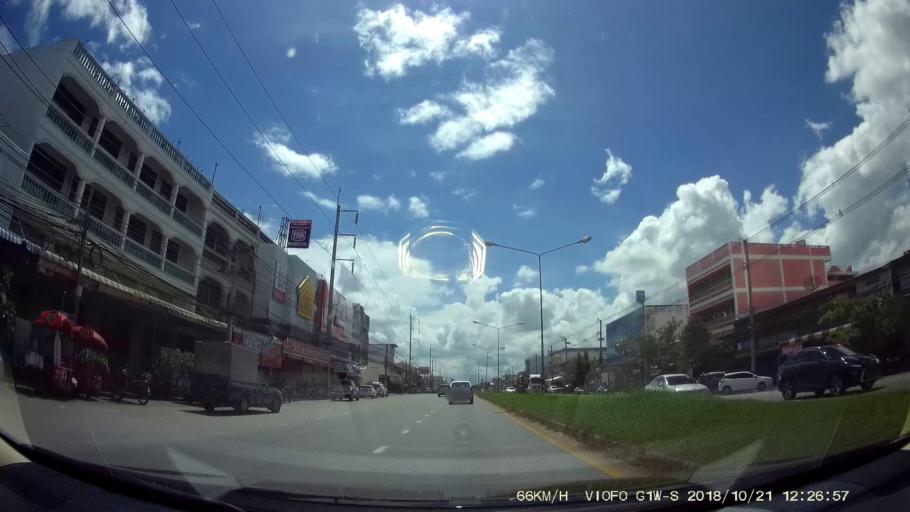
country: TH
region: Nakhon Ratchasima
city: Dan Khun Thot
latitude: 15.2064
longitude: 101.7663
